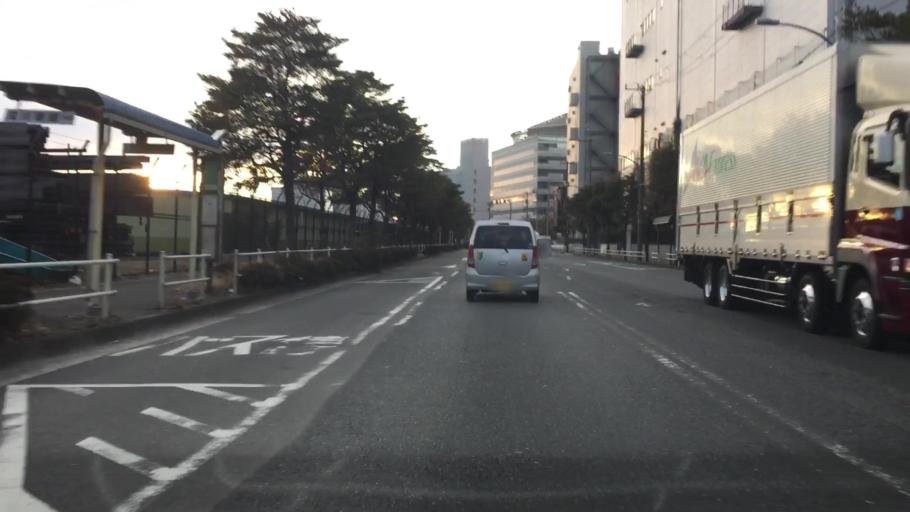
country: JP
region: Tokyo
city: Urayasu
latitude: 35.6421
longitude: 139.8126
